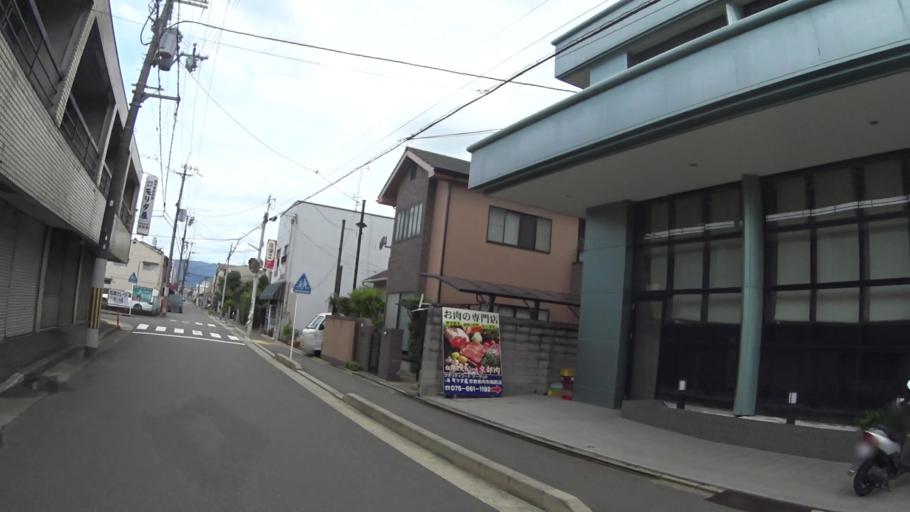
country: JP
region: Kyoto
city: Muko
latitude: 34.9650
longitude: 135.7313
